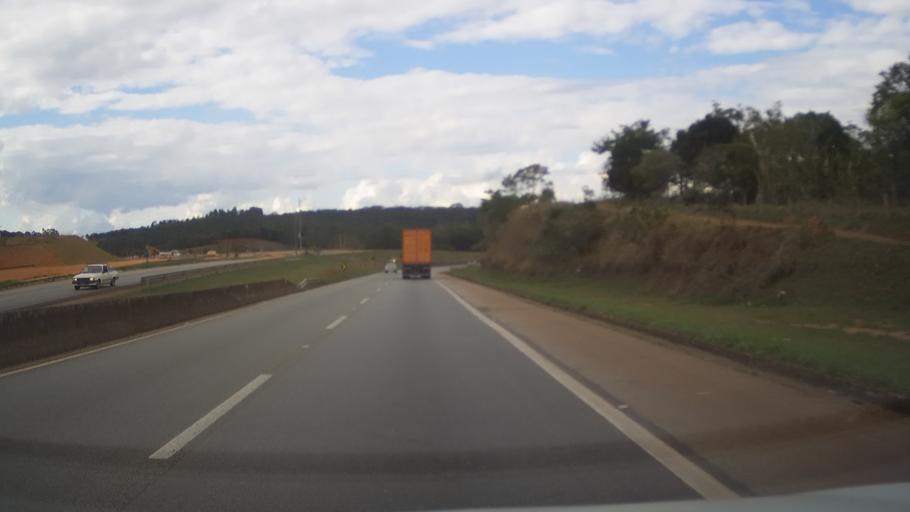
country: BR
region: Minas Gerais
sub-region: Itauna
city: Itauna
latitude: -20.2882
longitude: -44.4356
